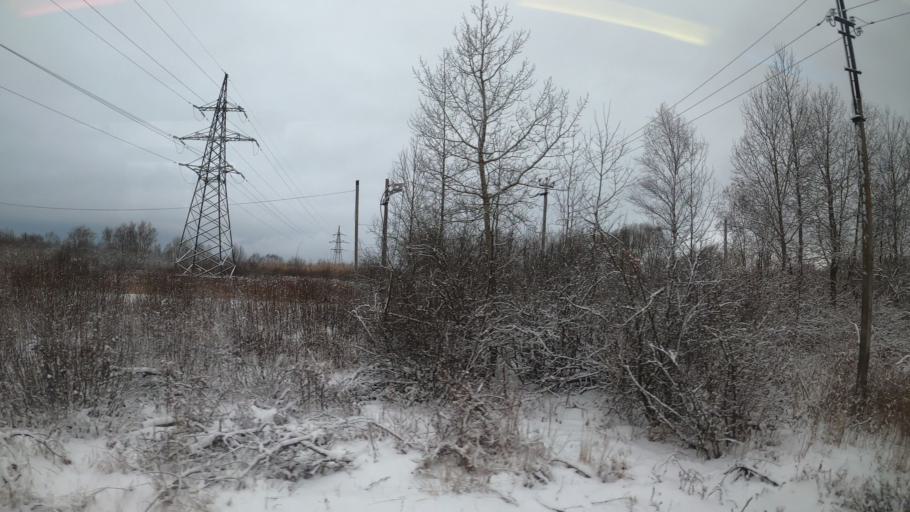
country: RU
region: Jaroslavl
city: Pereslavl'-Zalesskiy
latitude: 56.7315
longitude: 38.9003
